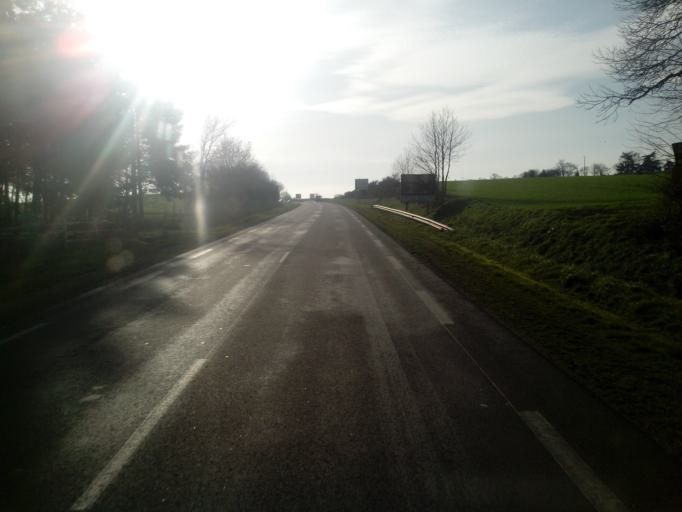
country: FR
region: Brittany
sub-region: Departement du Morbihan
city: Mauron
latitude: 48.1004
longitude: -2.2638
